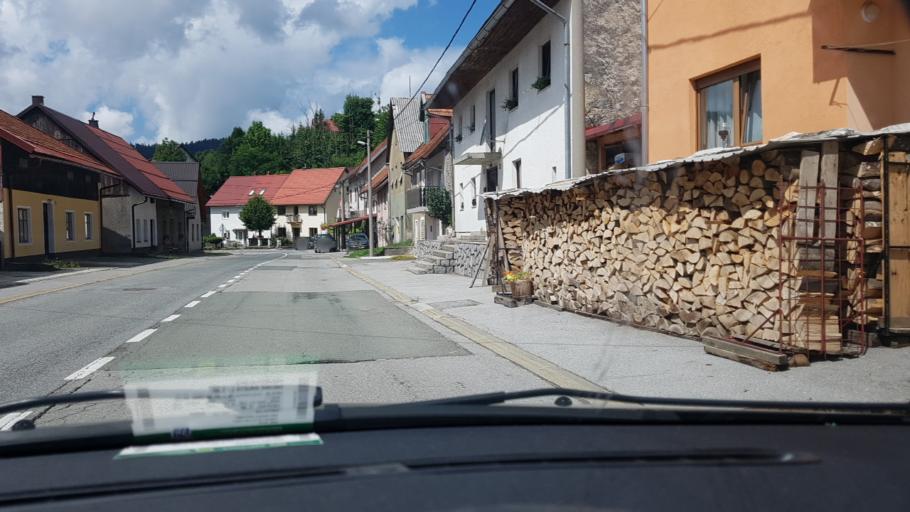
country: HR
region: Primorsko-Goranska
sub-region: Grad Delnice
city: Delnice
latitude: 45.3586
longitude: 14.7508
